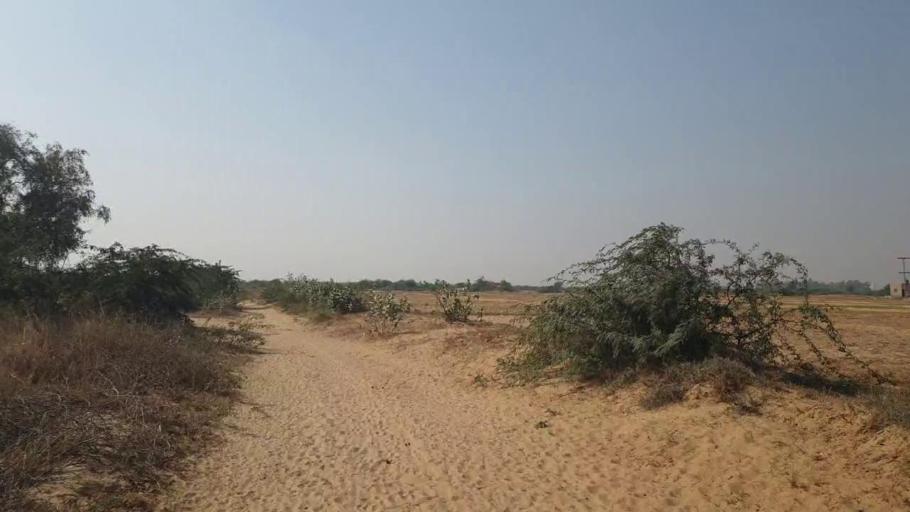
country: PK
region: Sindh
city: Kotri
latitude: 25.3103
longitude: 68.2974
